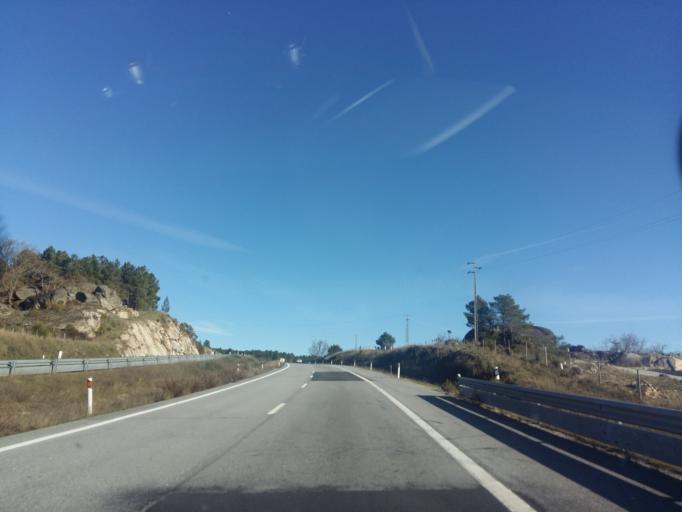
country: PT
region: Guarda
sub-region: Guarda
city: Sequeira
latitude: 40.5776
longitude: -7.1823
